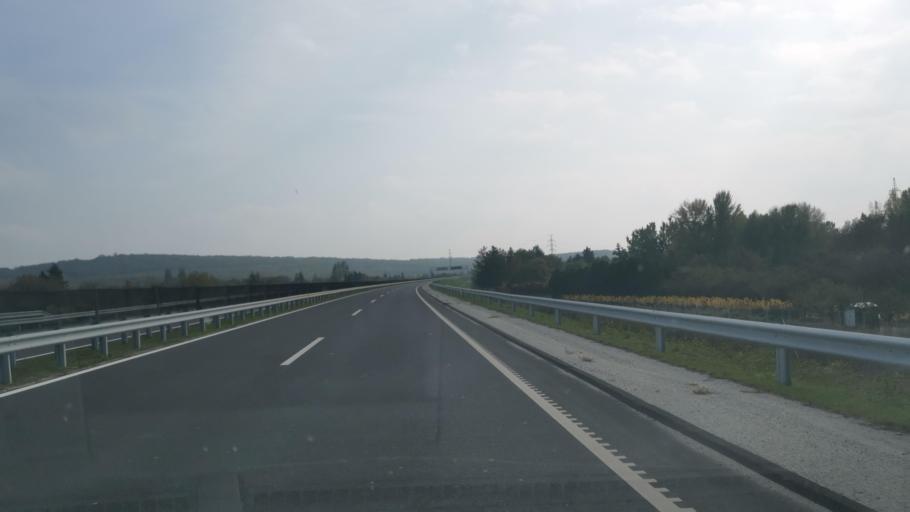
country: HU
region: Gyor-Moson-Sopron
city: Sopron
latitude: 47.6980
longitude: 16.6170
